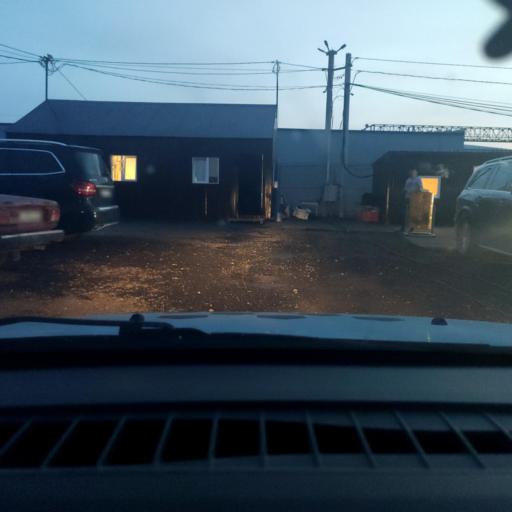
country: RU
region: Perm
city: Gamovo
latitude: 57.9085
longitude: 56.1822
